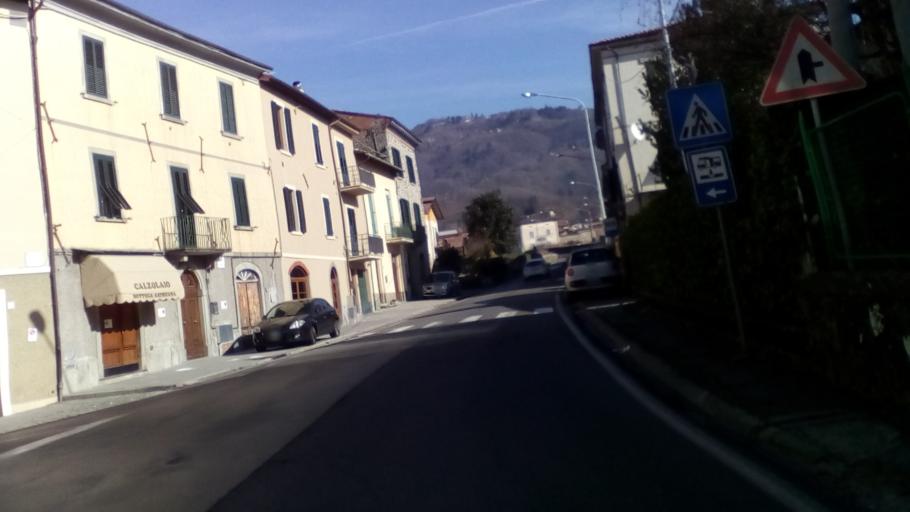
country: IT
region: Tuscany
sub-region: Provincia di Lucca
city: Pieve Fosciana
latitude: 44.1334
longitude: 10.4139
